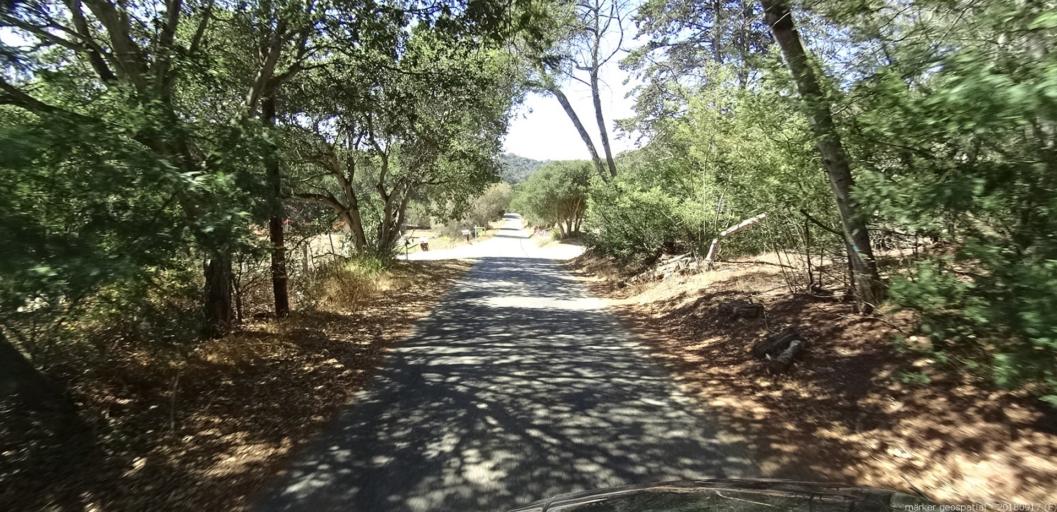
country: US
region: California
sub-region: Monterey County
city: Elkhorn
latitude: 36.8295
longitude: -121.6960
